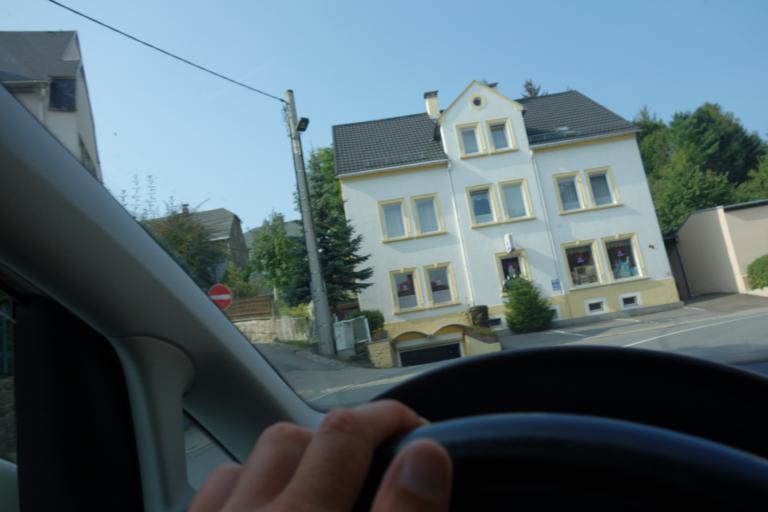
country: DE
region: Saxony
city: Grunhainichen
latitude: 50.7674
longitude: 13.1532
